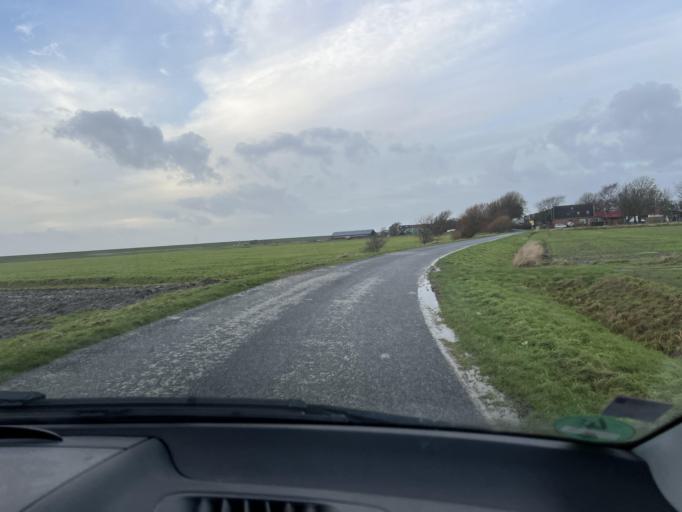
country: DE
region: Schleswig-Holstein
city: Hedwigenkoog
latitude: 54.1758
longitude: 8.8207
